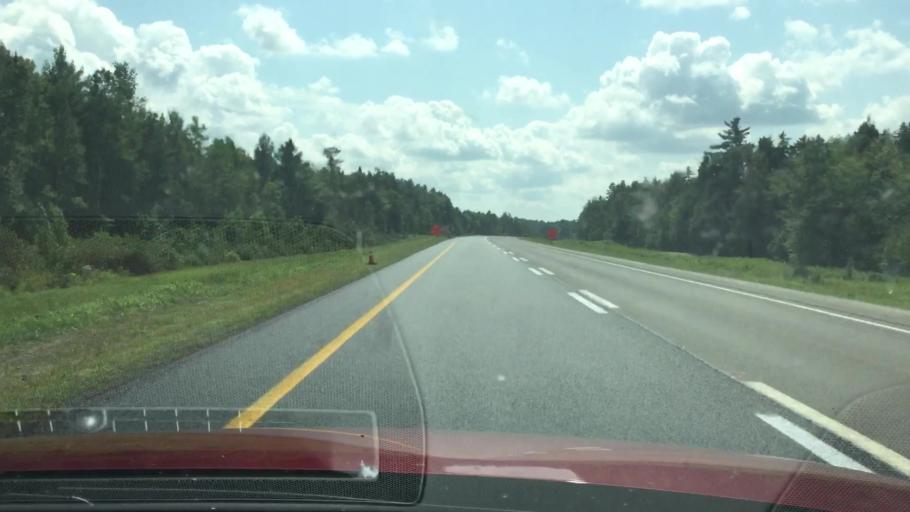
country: US
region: Maine
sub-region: Penobscot County
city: Medway
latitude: 45.6936
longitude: -68.4878
